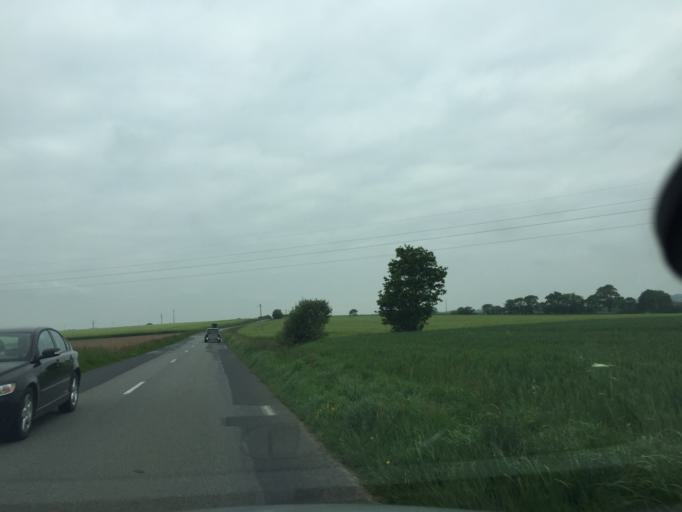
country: FR
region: Brittany
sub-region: Departement des Cotes-d'Armor
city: Henanbihen
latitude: 48.5376
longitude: -2.4040
